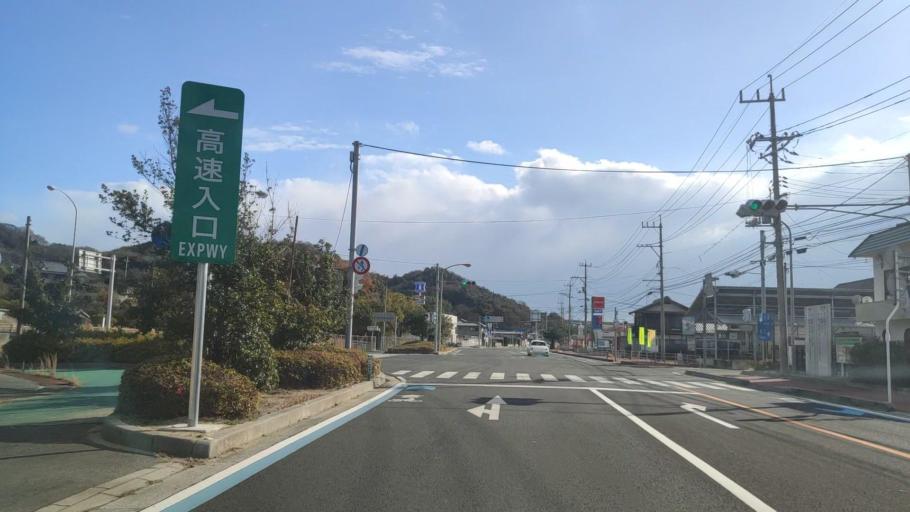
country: JP
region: Hiroshima
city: Innoshima
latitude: 34.2054
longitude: 133.0750
